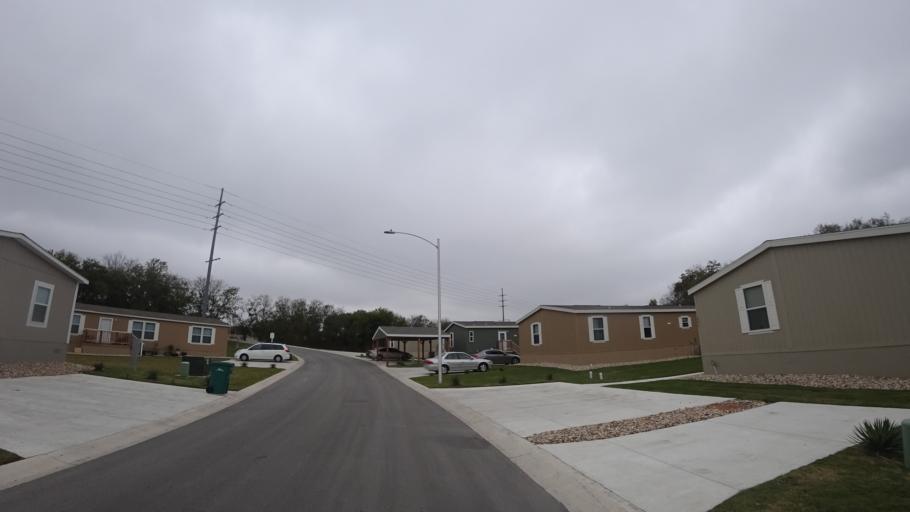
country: US
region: Texas
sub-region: Travis County
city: Pflugerville
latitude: 30.3924
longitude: -97.6380
